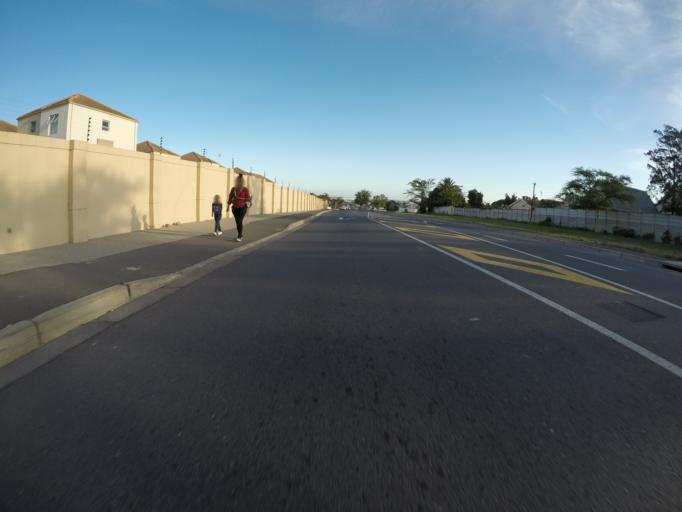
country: ZA
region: Western Cape
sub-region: City of Cape Town
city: Kraaifontein
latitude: -33.8626
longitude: 18.6832
